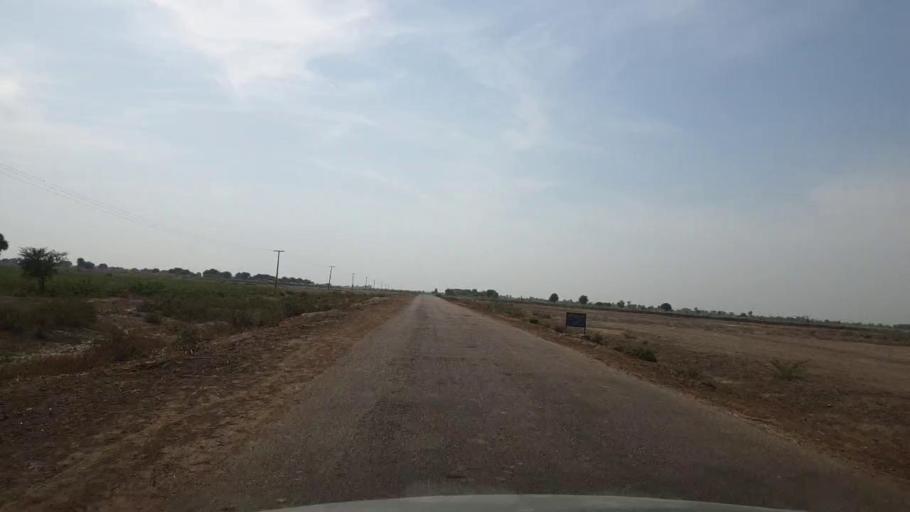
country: PK
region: Sindh
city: Kunri
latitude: 25.1582
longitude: 69.4926
